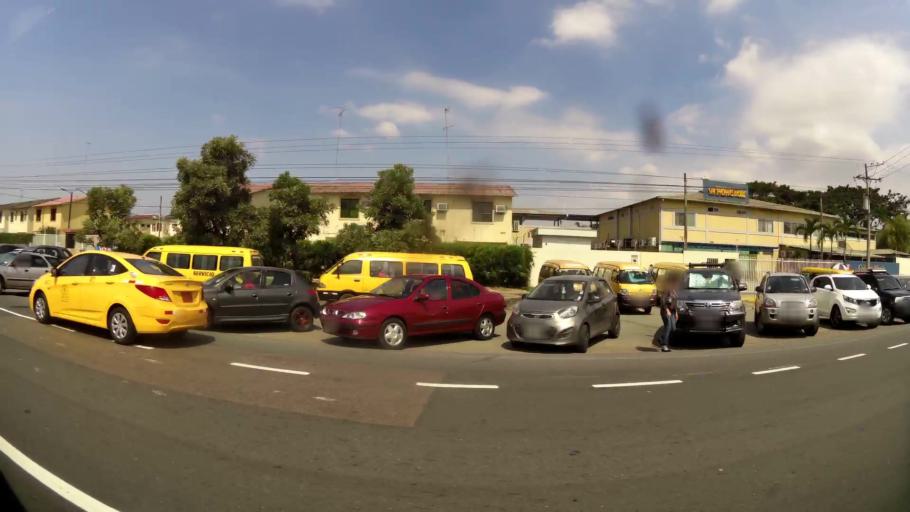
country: EC
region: Guayas
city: El Triunfo
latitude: -2.0491
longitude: -79.9112
